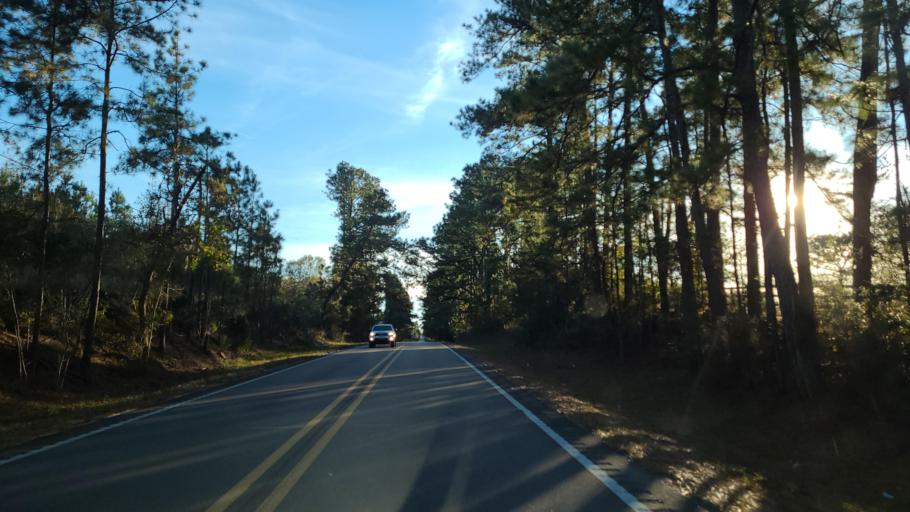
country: US
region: Mississippi
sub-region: Lamar County
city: Lumberton
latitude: 31.0526
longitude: -89.4311
